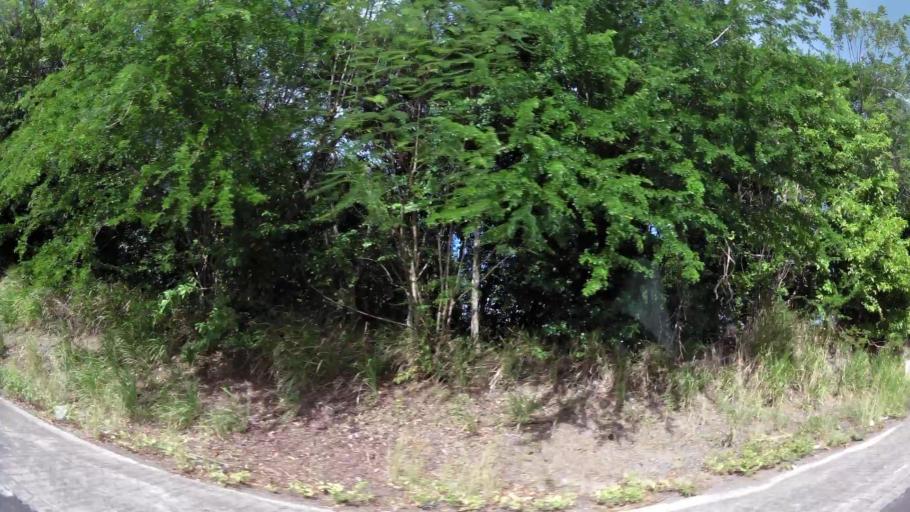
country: MQ
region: Martinique
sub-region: Martinique
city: Les Trois-Ilets
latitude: 14.5339
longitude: -61.0260
